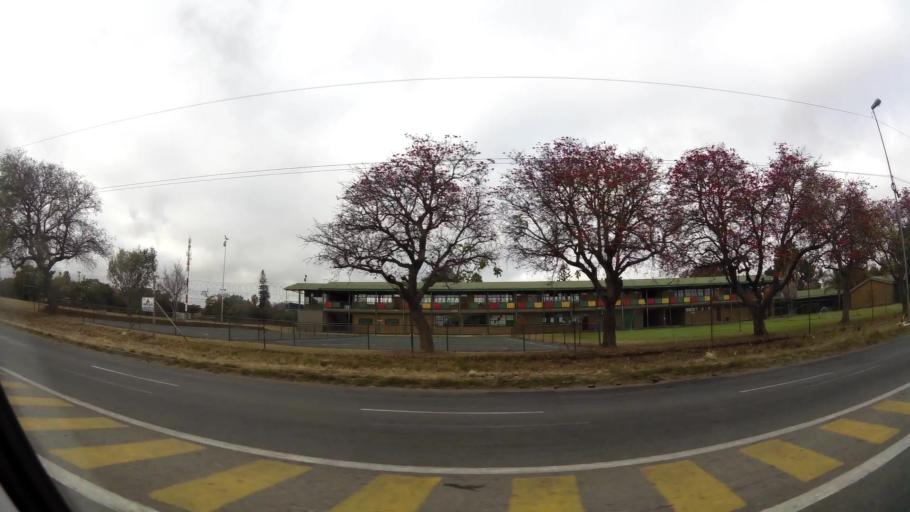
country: ZA
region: Limpopo
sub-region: Capricorn District Municipality
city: Polokwane
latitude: -23.8742
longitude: 29.4493
